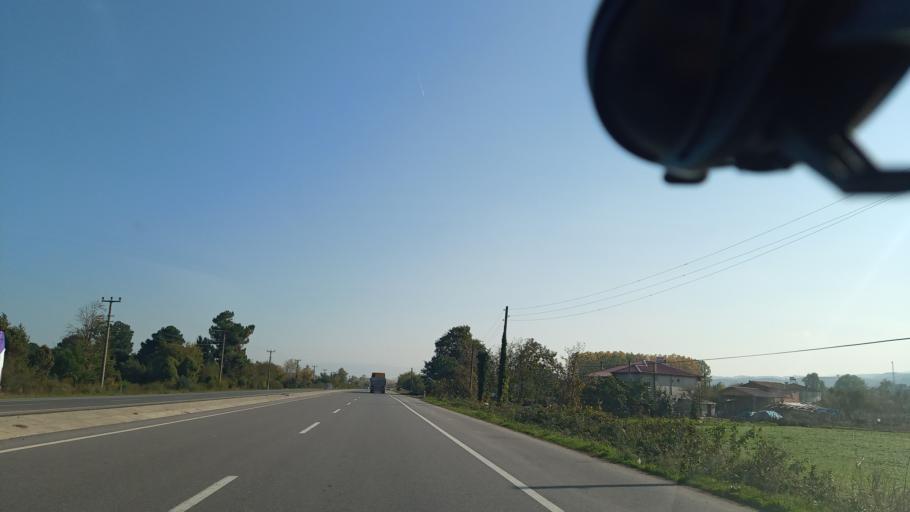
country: TR
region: Sakarya
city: Karasu
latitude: 41.0790
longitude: 30.7734
